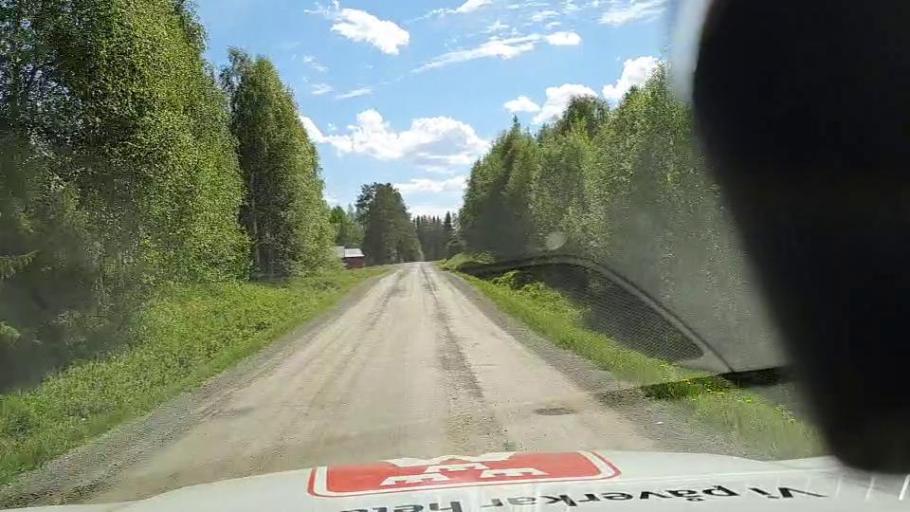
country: SE
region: Jaemtland
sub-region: Stroemsunds Kommun
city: Stroemsund
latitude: 64.4572
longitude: 15.5908
